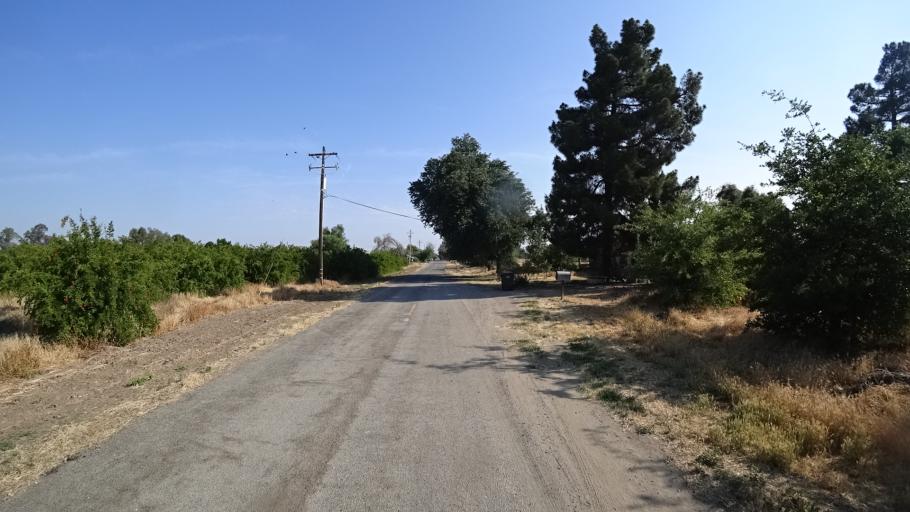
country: US
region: California
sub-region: Kings County
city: Lemoore
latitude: 36.3609
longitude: -119.8161
